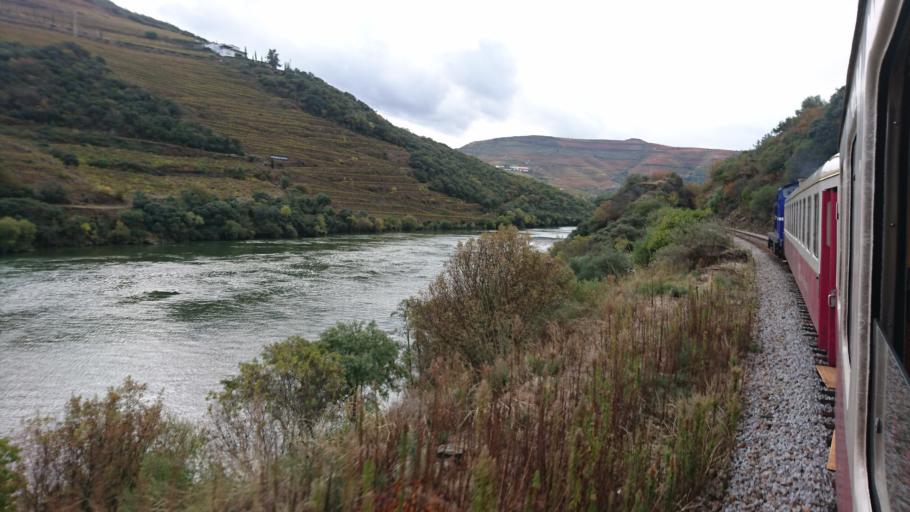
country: PT
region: Vila Real
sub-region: Sabrosa
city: Sabrosa
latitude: 41.1973
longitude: -7.5104
